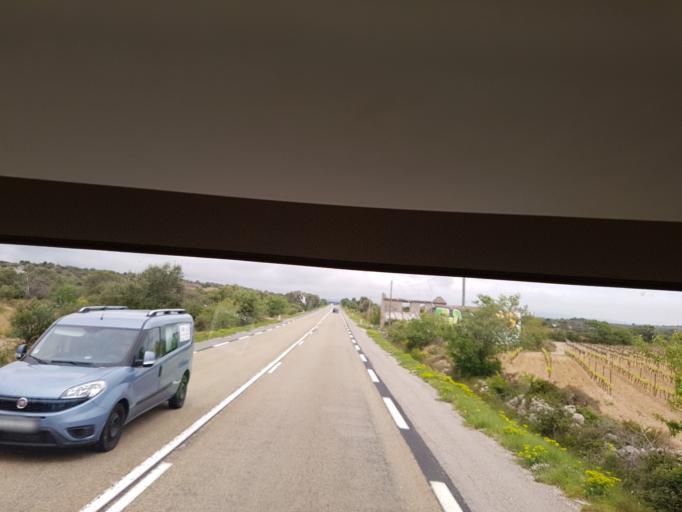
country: FR
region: Languedoc-Roussillon
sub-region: Departement de l'Aude
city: Leucate
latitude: 42.9089
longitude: 2.9994
